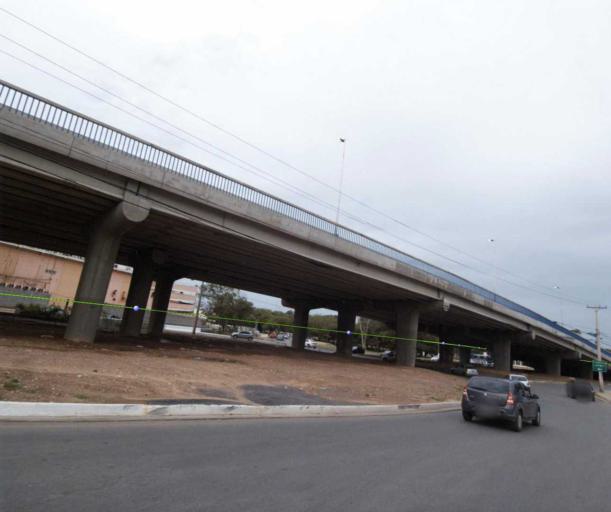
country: BR
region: Mato Grosso
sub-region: Cuiaba
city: Cuiaba
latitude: -15.6138
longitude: -56.0748
